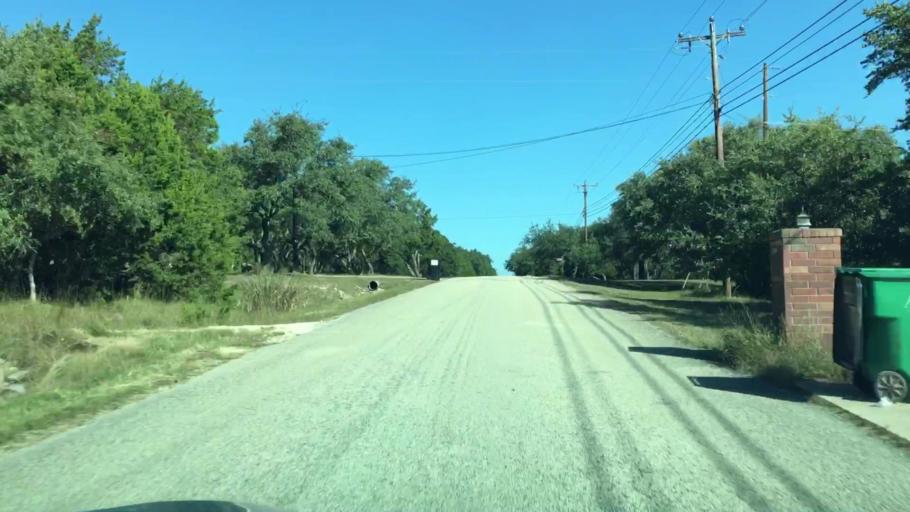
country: US
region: Texas
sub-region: Hays County
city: Dripping Springs
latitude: 30.1938
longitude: -98.0193
